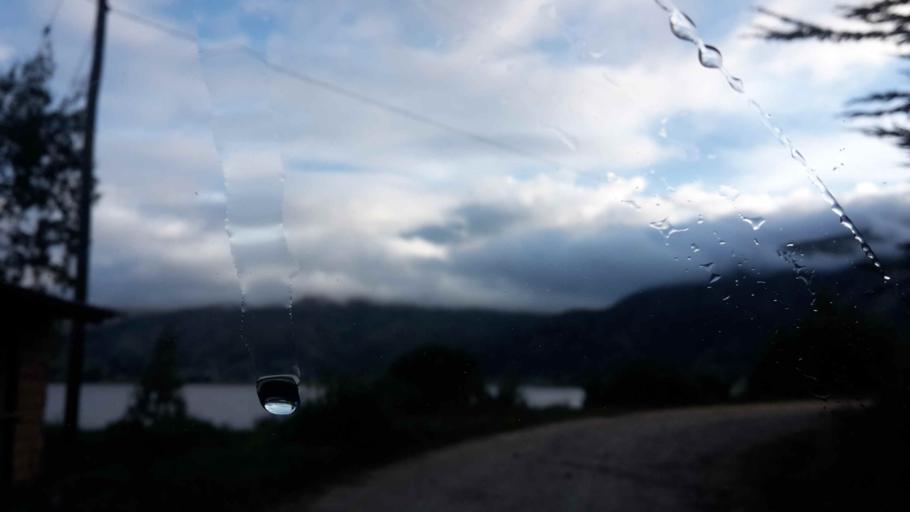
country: BO
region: Cochabamba
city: Colomi
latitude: -17.2781
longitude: -65.9104
